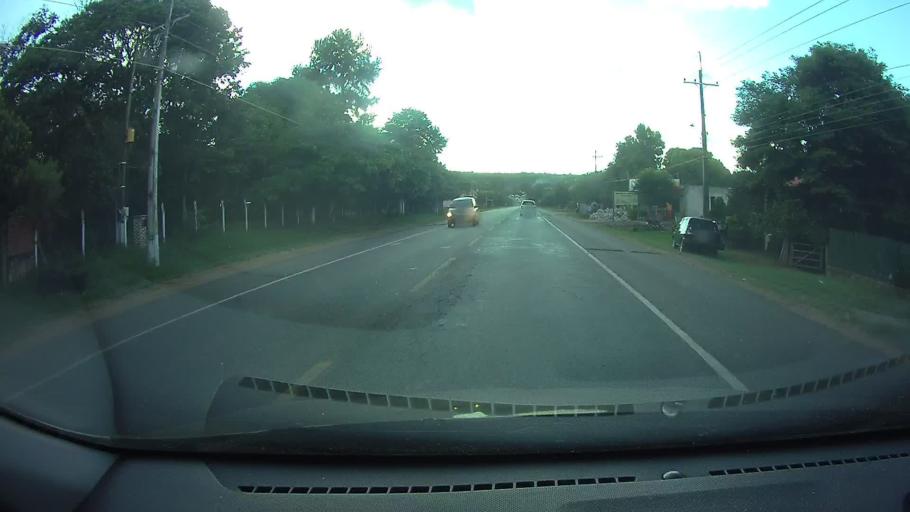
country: PY
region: Cordillera
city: Eusebio Ayala
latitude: -25.3781
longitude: -57.0221
